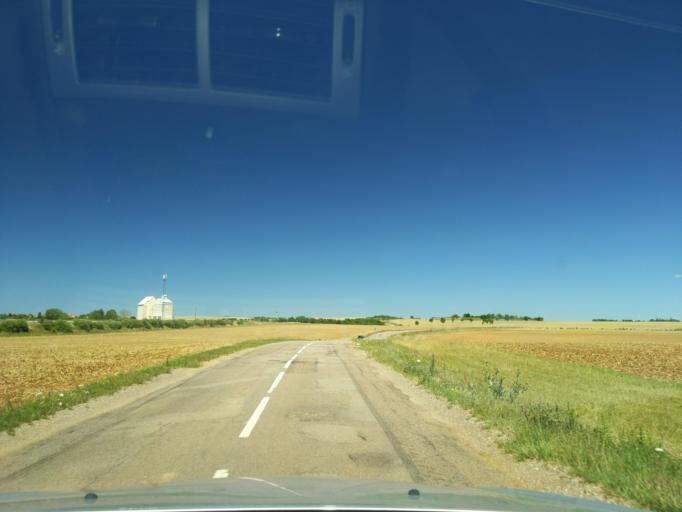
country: FR
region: Bourgogne
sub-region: Departement de la Cote-d'Or
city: Is-sur-Tille
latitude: 47.4649
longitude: 5.0841
